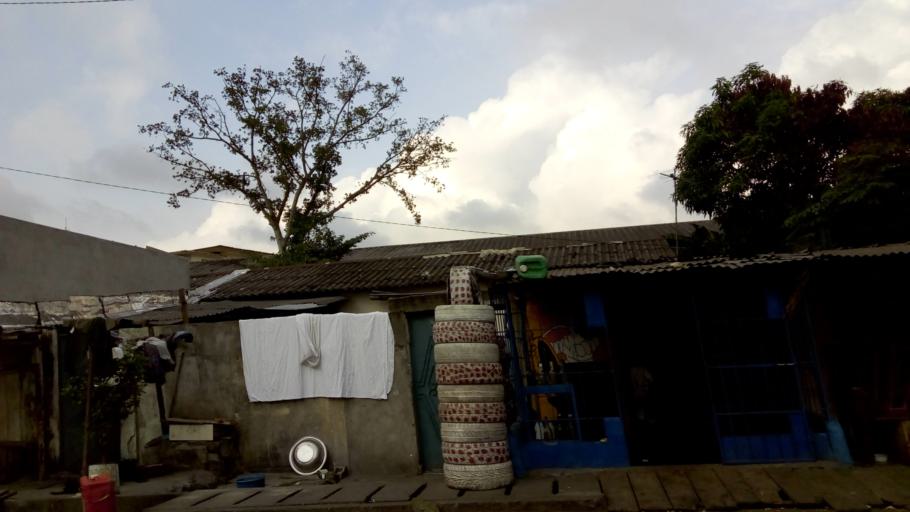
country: CI
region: Lagunes
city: Abidjan
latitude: 5.3373
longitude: -4.0256
